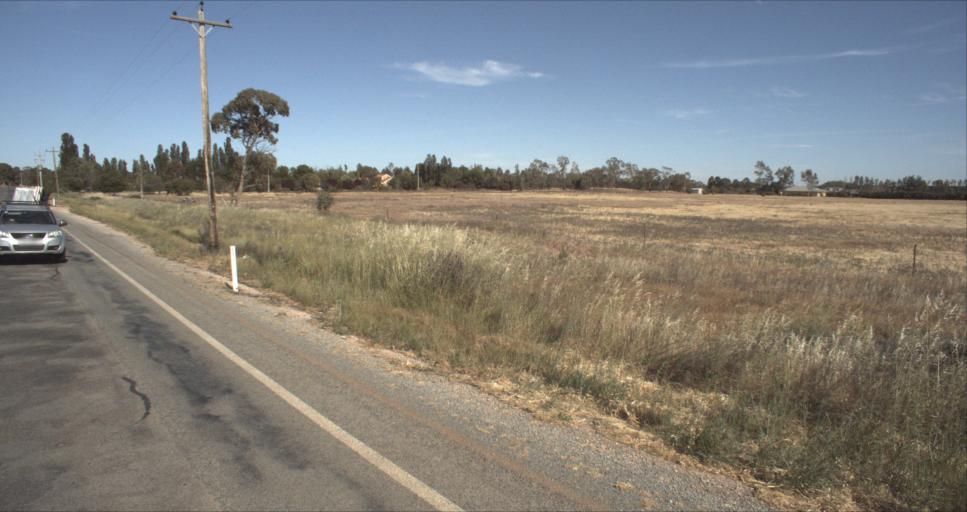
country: AU
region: New South Wales
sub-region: Leeton
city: Leeton
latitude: -34.5632
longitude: 146.4298
